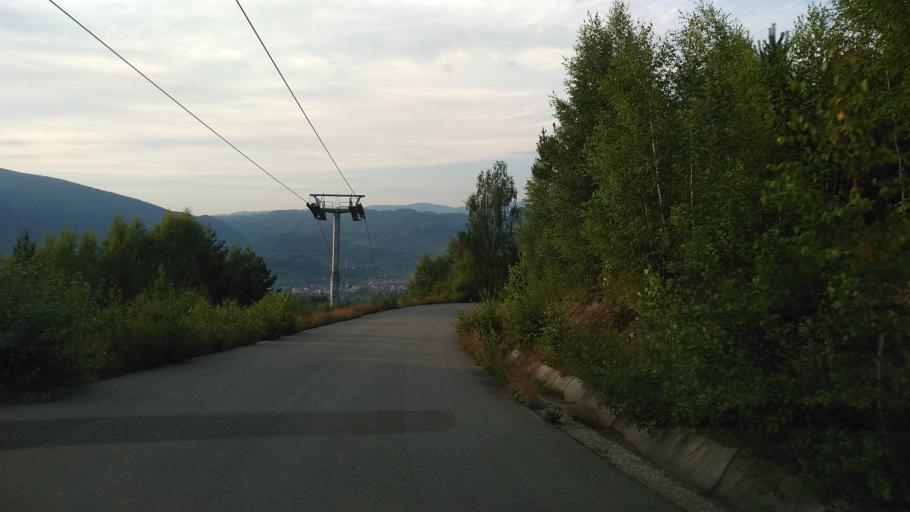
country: RO
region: Hunedoara
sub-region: Municipiul  Vulcan
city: Jiu-Paroseni
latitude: 45.3504
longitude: 23.2899
